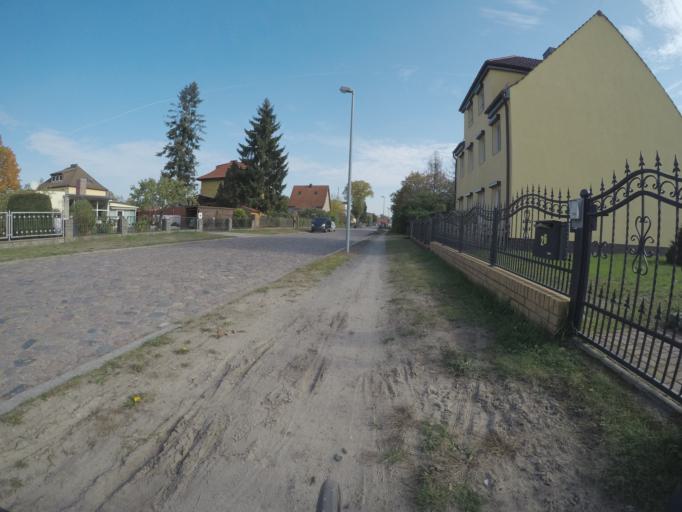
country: DE
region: Brandenburg
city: Oranienburg
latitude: 52.7508
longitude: 13.2129
